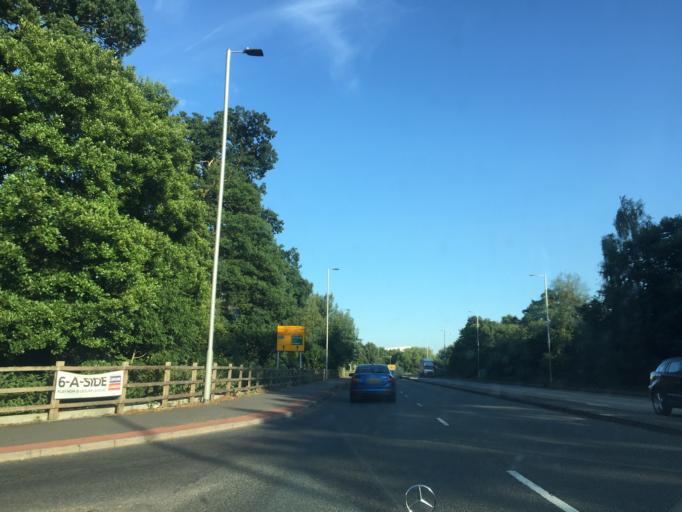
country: GB
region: England
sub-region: Bracknell Forest
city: Sandhurst
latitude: 51.3352
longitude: -0.7769
